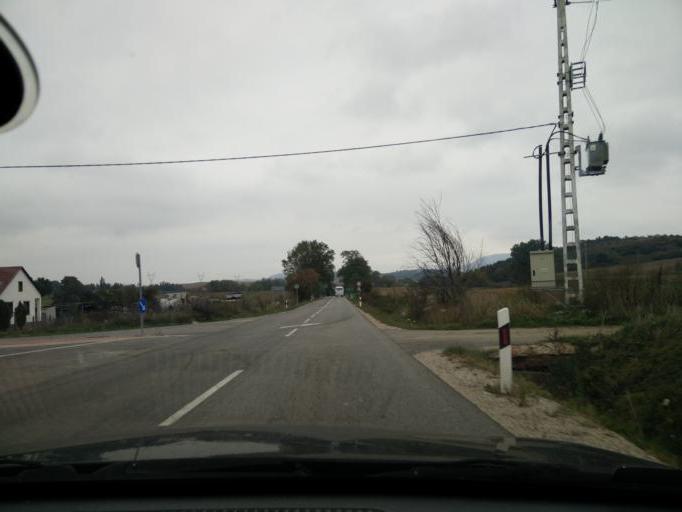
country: HU
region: Komarom-Esztergom
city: Bajna
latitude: 47.6766
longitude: 18.6081
